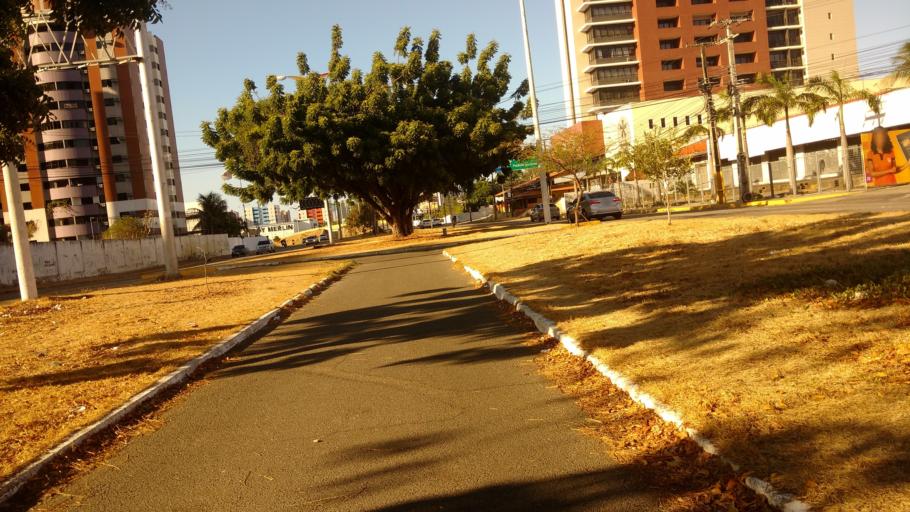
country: BR
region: Ceara
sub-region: Fortaleza
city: Fortaleza
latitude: -3.7622
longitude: -38.4828
